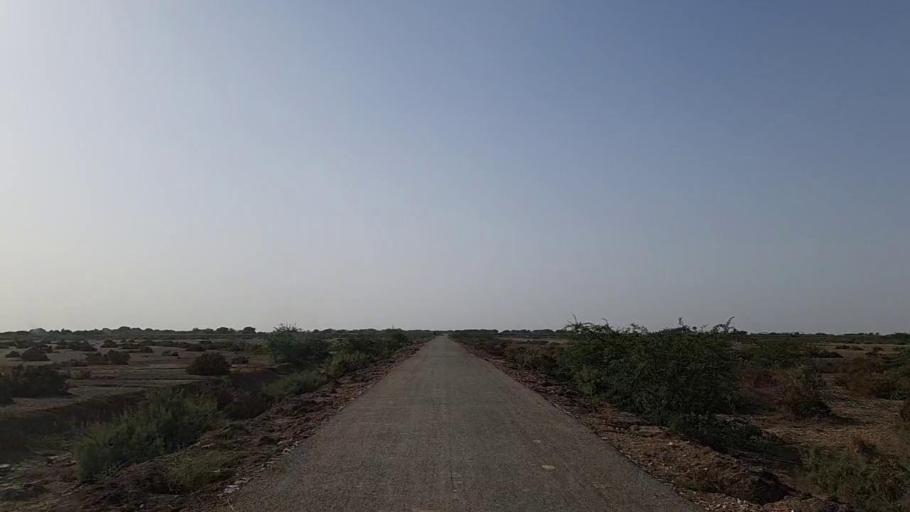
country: PK
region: Sindh
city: Jati
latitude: 24.3023
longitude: 68.1984
